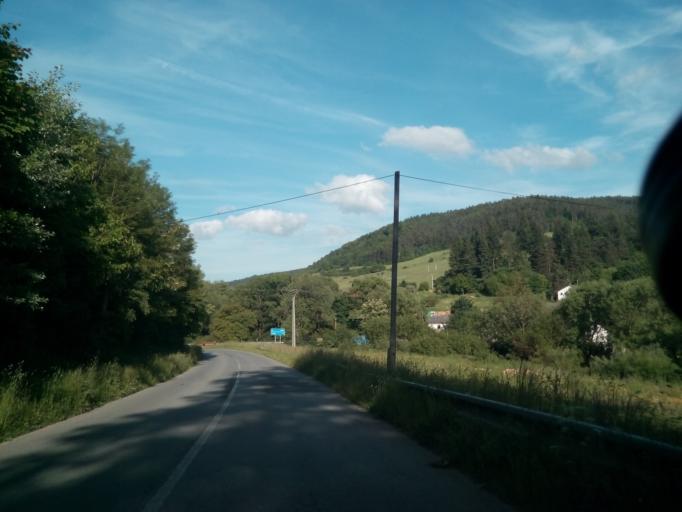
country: SK
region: Presovsky
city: Lipany
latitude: 49.0179
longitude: 20.9745
